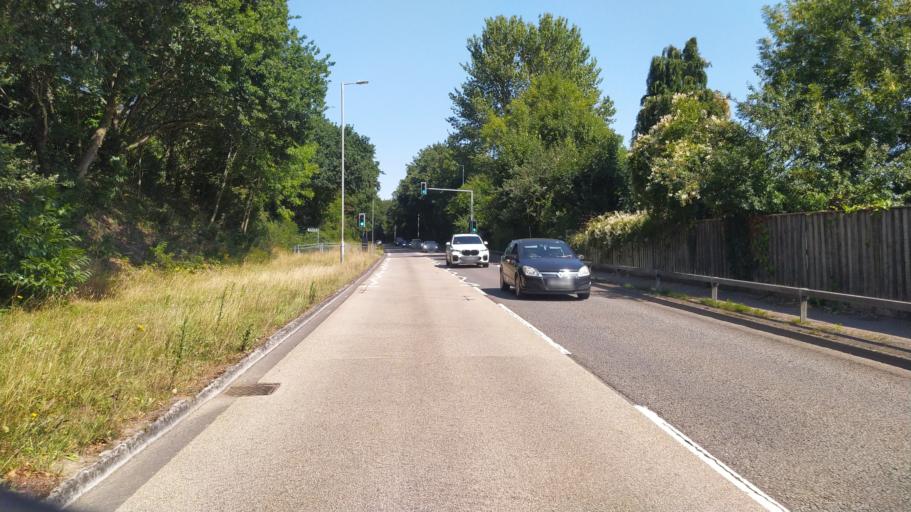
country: GB
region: England
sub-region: Dorset
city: Broadstone
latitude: 50.7533
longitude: -2.0017
